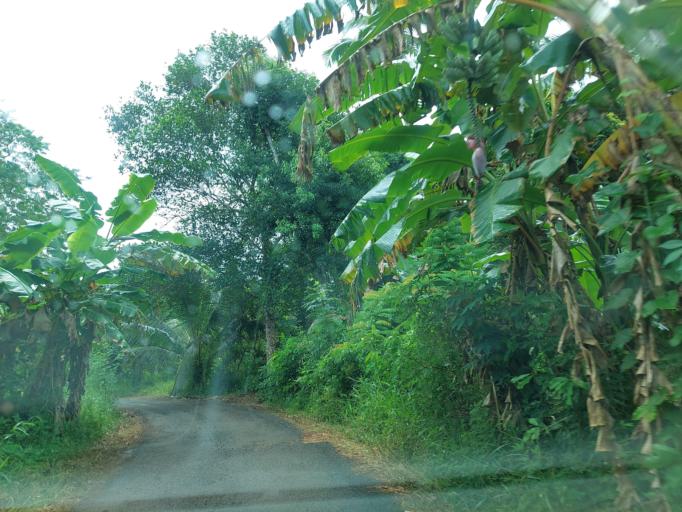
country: YT
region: Tsingoni
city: Tsingoni
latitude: -12.7549
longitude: 45.1248
